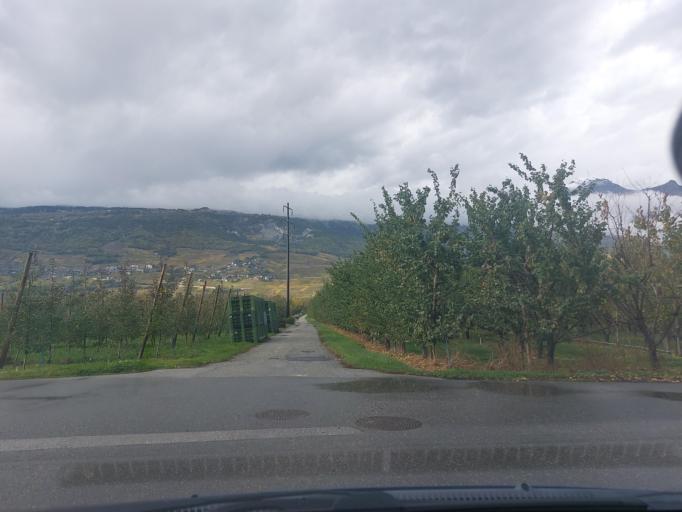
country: CH
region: Valais
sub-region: Sierre District
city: Chalais
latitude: 46.2756
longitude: 7.5220
